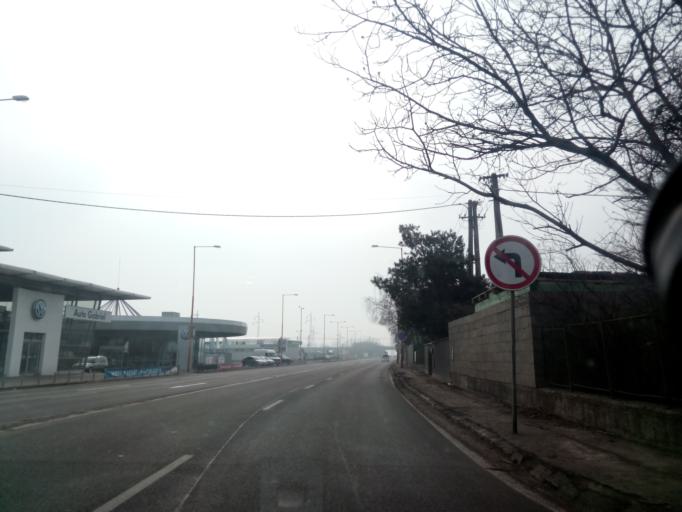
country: SK
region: Kosicky
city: Kosice
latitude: 48.6710
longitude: 21.2708
